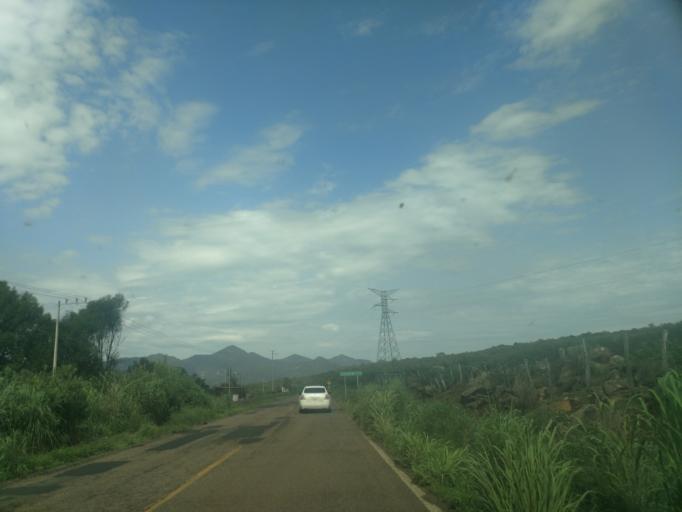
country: MX
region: Jalisco
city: Talpa de Allende
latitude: 20.4227
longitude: -104.7279
